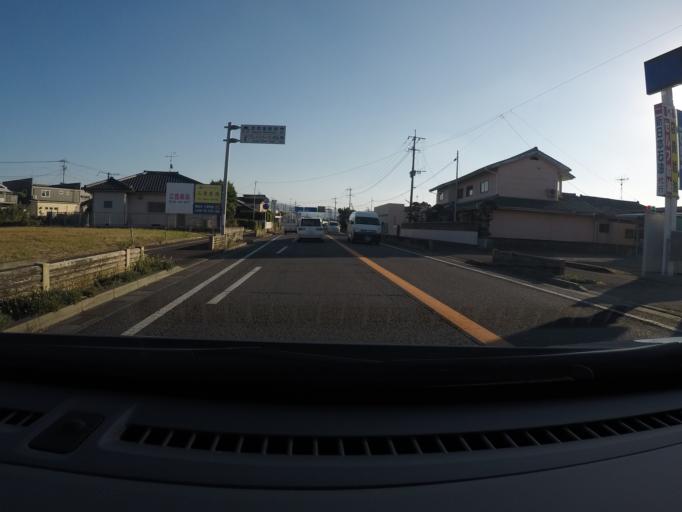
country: JP
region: Kagoshima
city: Izumi
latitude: 32.1194
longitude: 130.3400
